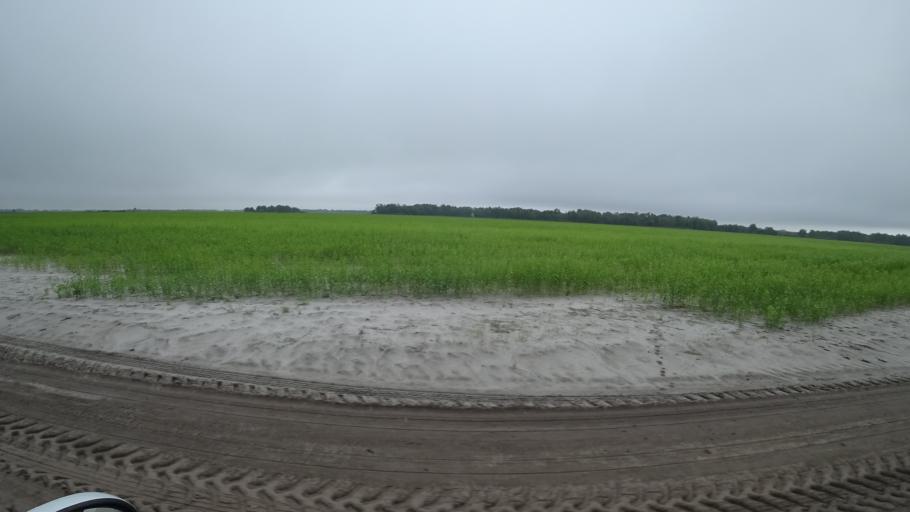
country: US
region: Florida
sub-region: Sarasota County
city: Warm Mineral Springs
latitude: 27.2872
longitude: -82.1677
